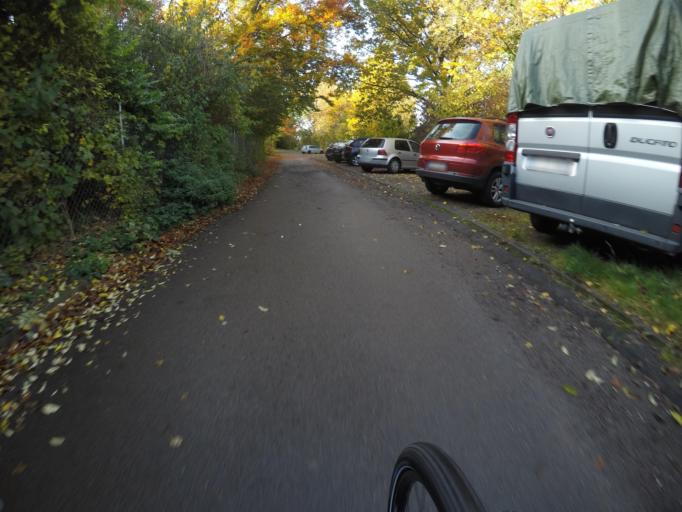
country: DE
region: Baden-Wuerttemberg
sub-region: Regierungsbezirk Stuttgart
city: Leinfelden-Echterdingen
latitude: 48.6842
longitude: 9.1497
